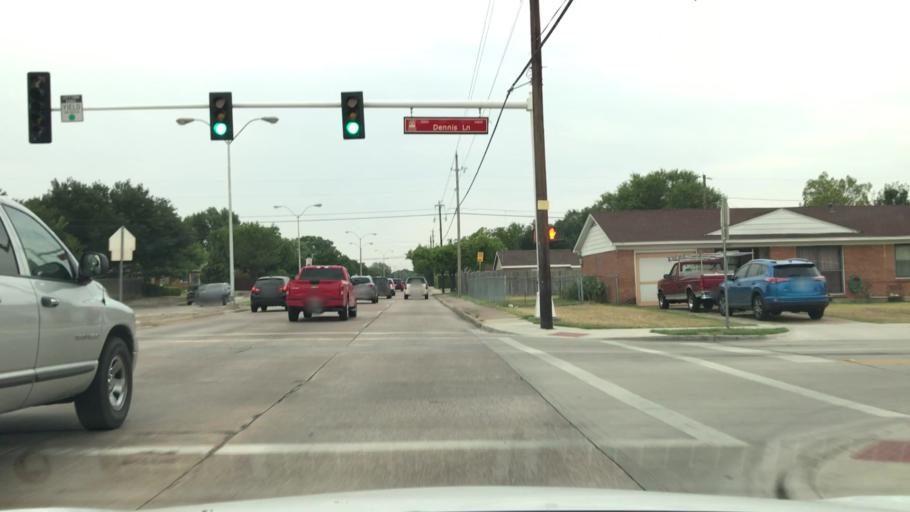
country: US
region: Texas
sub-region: Dallas County
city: Farmers Branch
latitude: 32.9336
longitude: -96.8883
